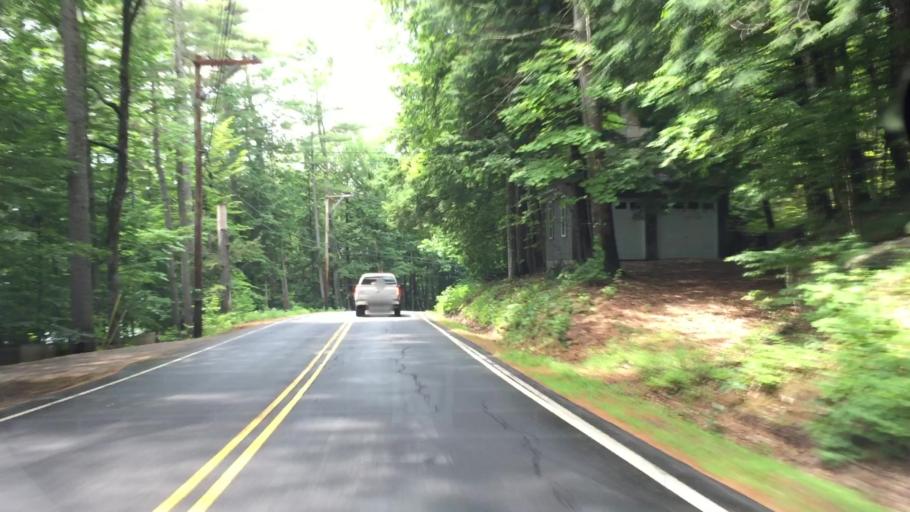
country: US
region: New Hampshire
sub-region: Grafton County
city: Holderness
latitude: 43.7435
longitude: -71.5684
